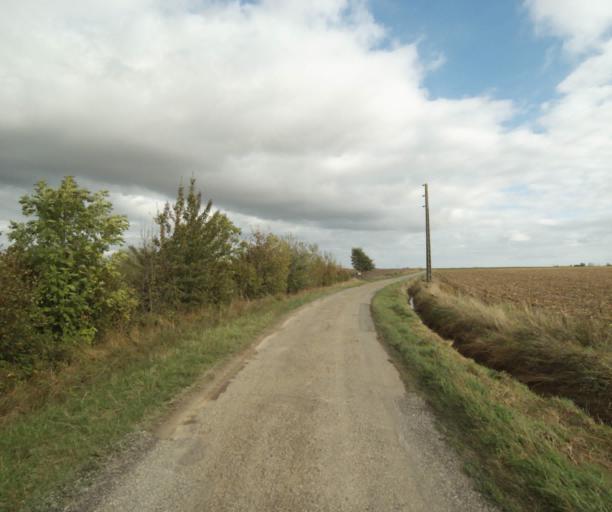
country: FR
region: Midi-Pyrenees
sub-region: Departement du Tarn-et-Garonne
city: Beaumont-de-Lomagne
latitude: 43.9067
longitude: 1.0971
